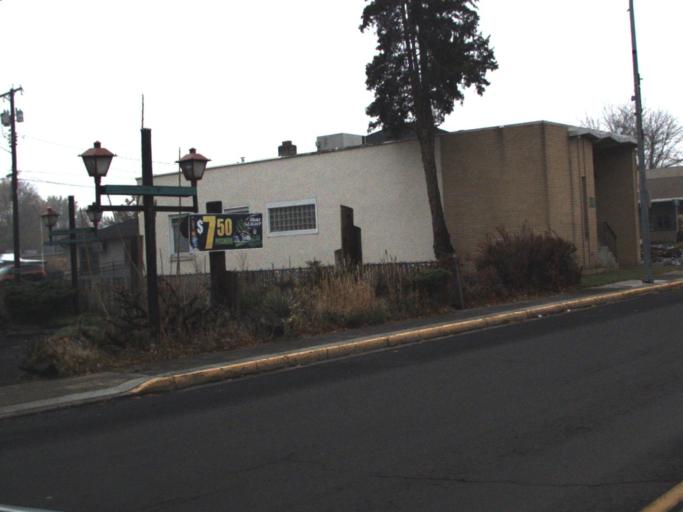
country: US
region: Washington
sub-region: Asotin County
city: Clarkston
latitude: 46.4156
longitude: -117.0456
